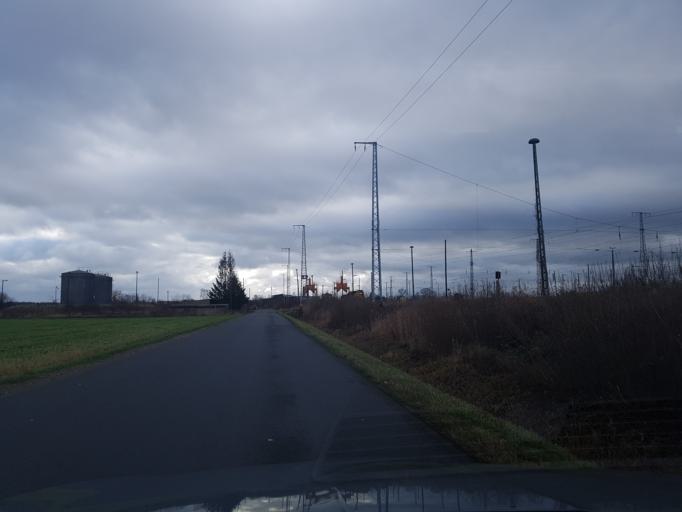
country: DE
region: Brandenburg
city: Falkenberg
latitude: 51.5945
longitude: 13.2444
